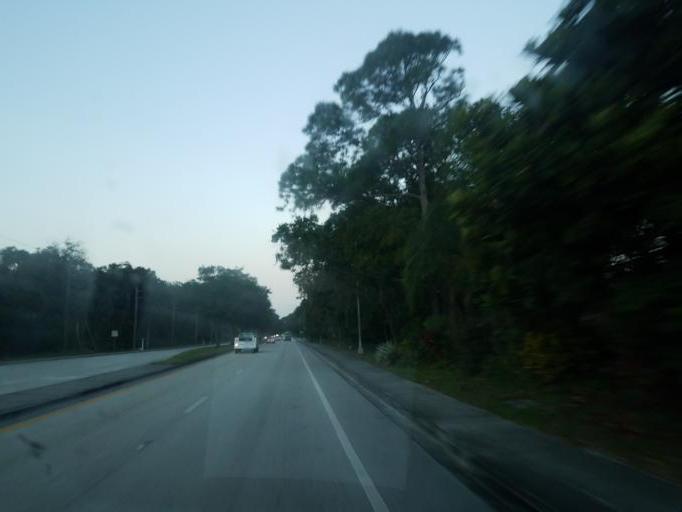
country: US
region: Florida
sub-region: Sarasota County
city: The Meadows
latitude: 27.3523
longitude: -82.4760
